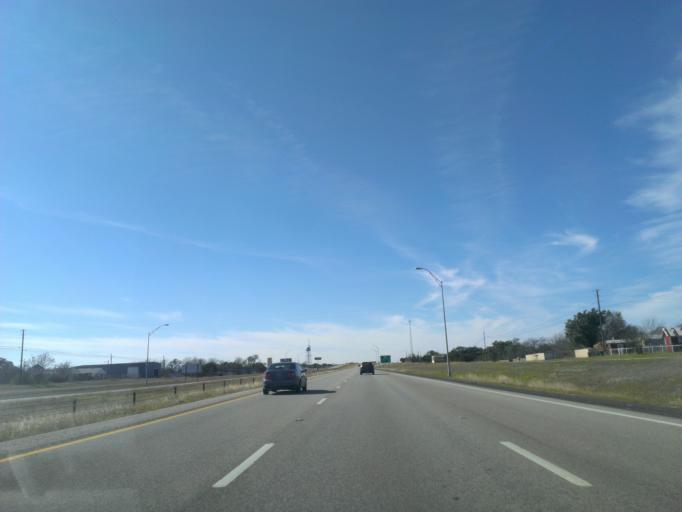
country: US
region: Texas
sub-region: Bell County
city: Nolanville
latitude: 31.0555
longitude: -97.5393
